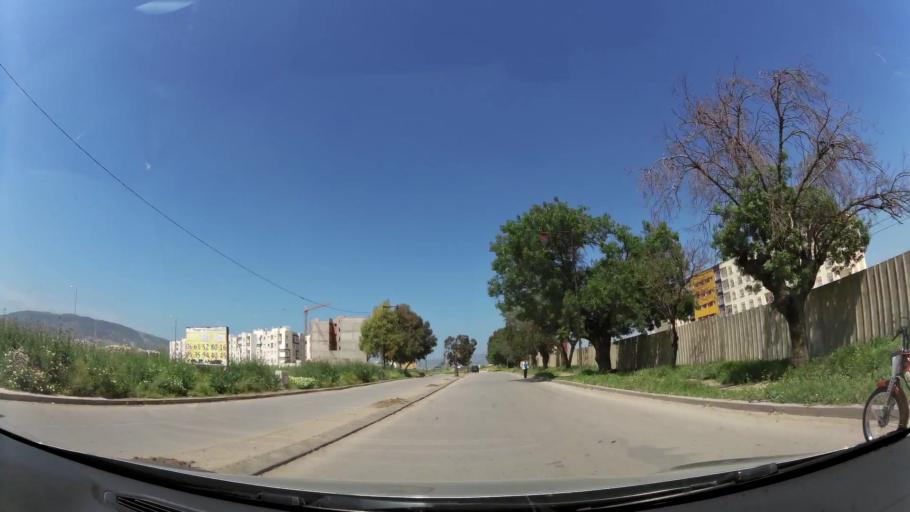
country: MA
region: Fes-Boulemane
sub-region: Fes
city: Fes
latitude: 34.0205
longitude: -5.0412
